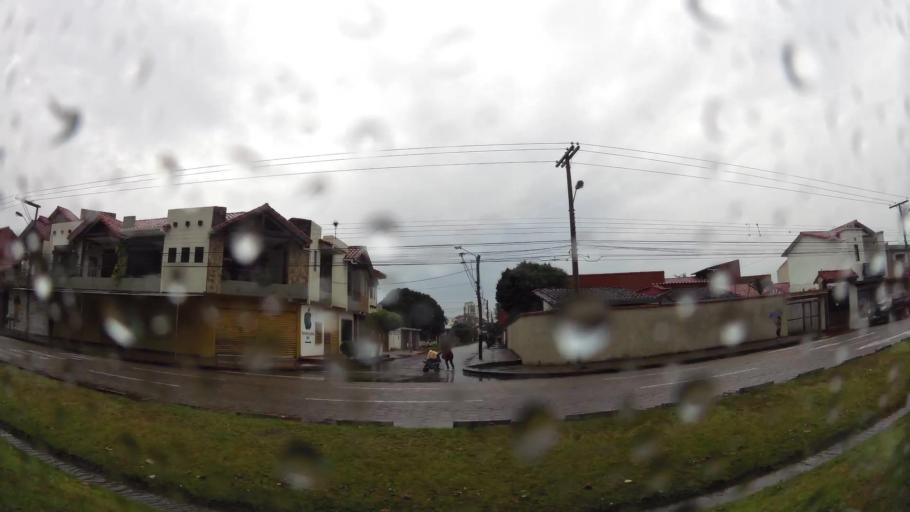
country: BO
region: Santa Cruz
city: Santa Cruz de la Sierra
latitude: -17.7911
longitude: -63.2120
